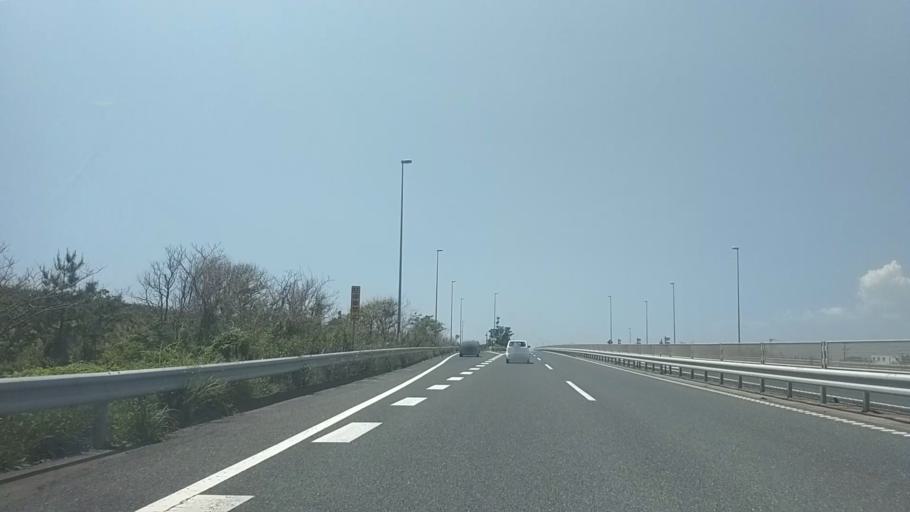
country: JP
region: Shizuoka
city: Hamamatsu
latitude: 34.6754
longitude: 137.6518
